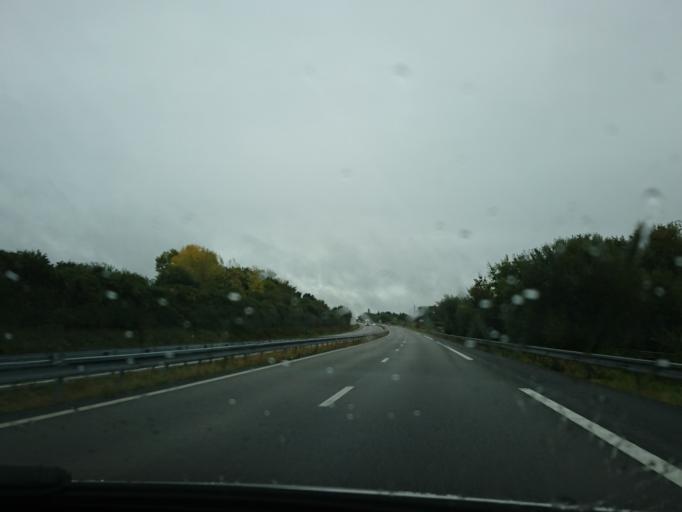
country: FR
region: Brittany
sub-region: Departement du Morbihan
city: Surzur
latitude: 47.6054
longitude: -2.6025
